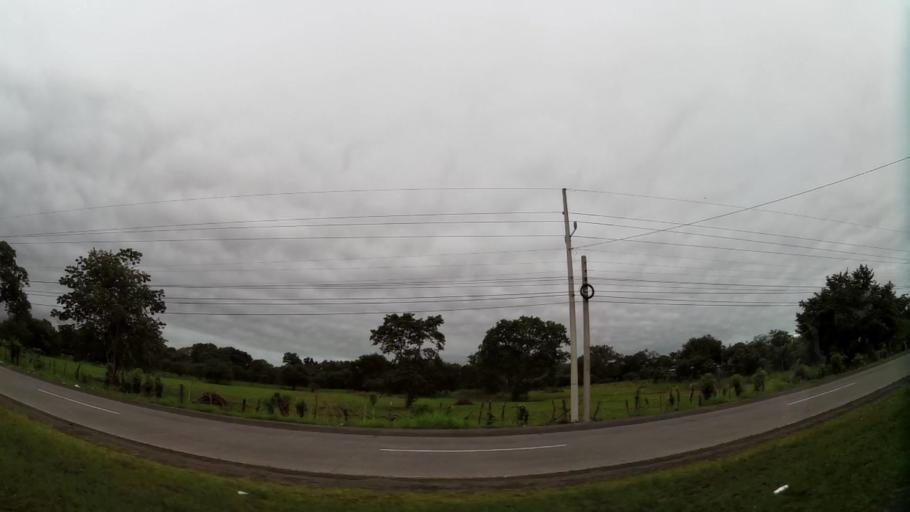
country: PA
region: Chiriqui
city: Tijera
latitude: 8.4760
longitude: -82.5490
